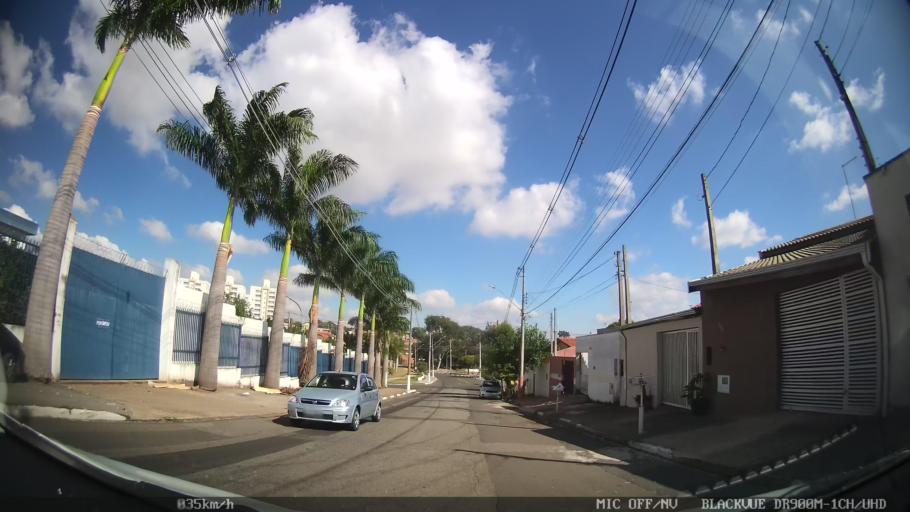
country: BR
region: Sao Paulo
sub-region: Hortolandia
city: Hortolandia
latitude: -22.8925
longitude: -47.1954
